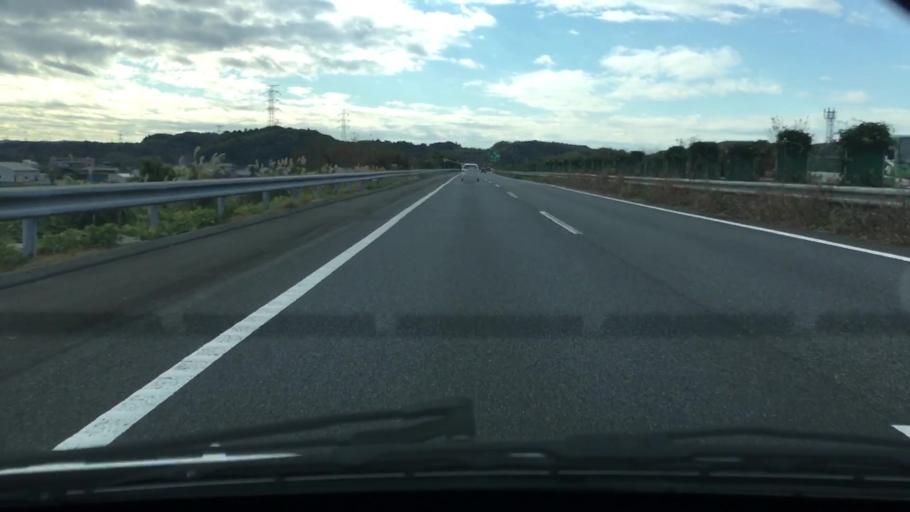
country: JP
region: Chiba
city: Kisarazu
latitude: 35.3981
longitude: 140.0059
